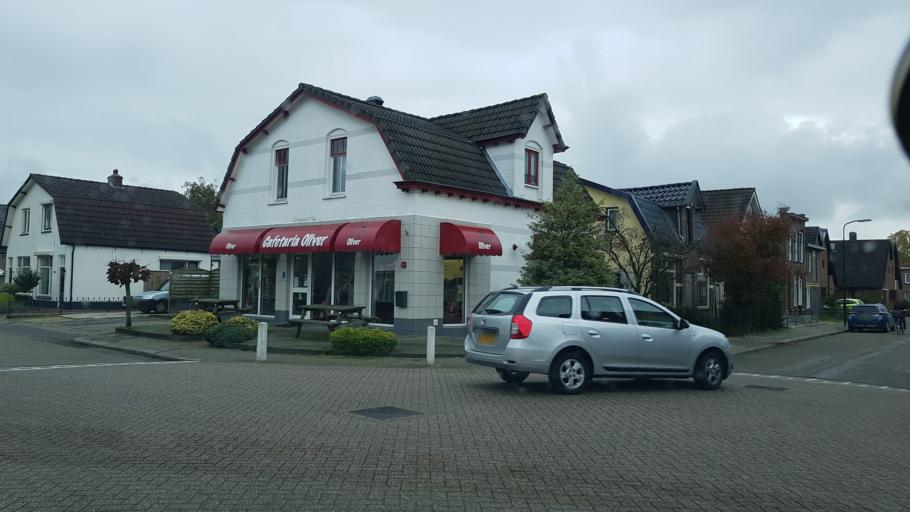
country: NL
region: Gelderland
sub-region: Gemeente Apeldoorn
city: Apeldoorn
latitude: 52.2177
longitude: 5.9768
